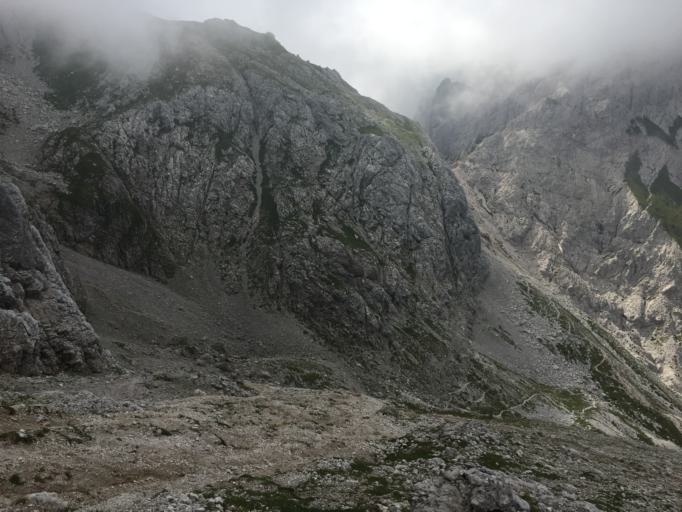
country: IT
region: Veneto
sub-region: Provincia di Belluno
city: Granvilla
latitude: 46.5421
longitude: 12.7309
